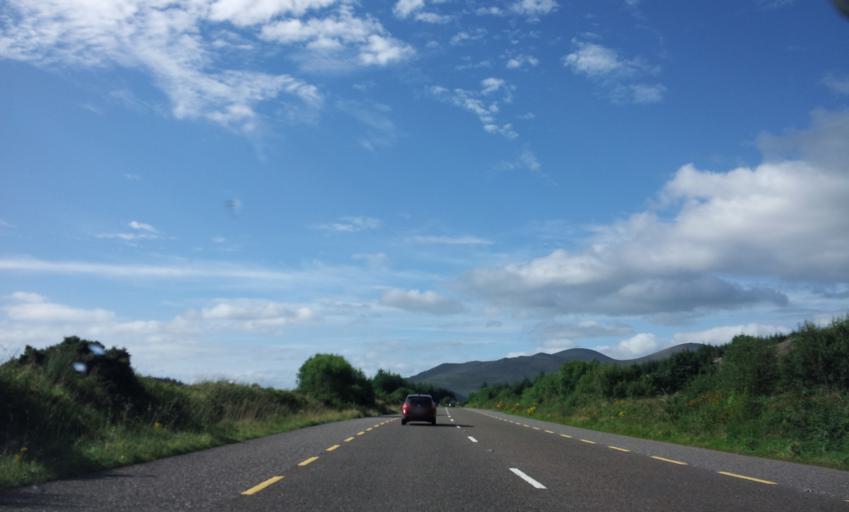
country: IE
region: Munster
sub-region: County Cork
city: Millstreet
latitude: 51.9661
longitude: -9.2486
